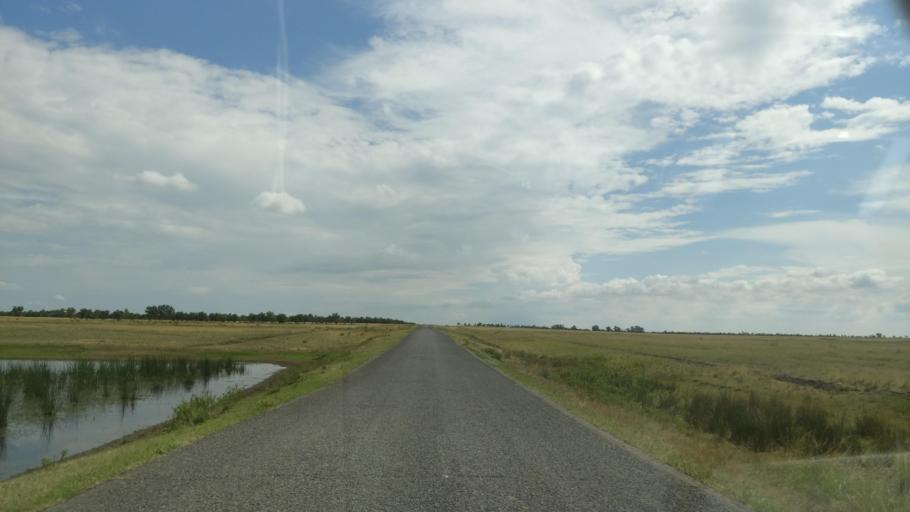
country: KZ
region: Pavlodar
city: Pavlodar
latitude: 52.6363
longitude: 76.9548
